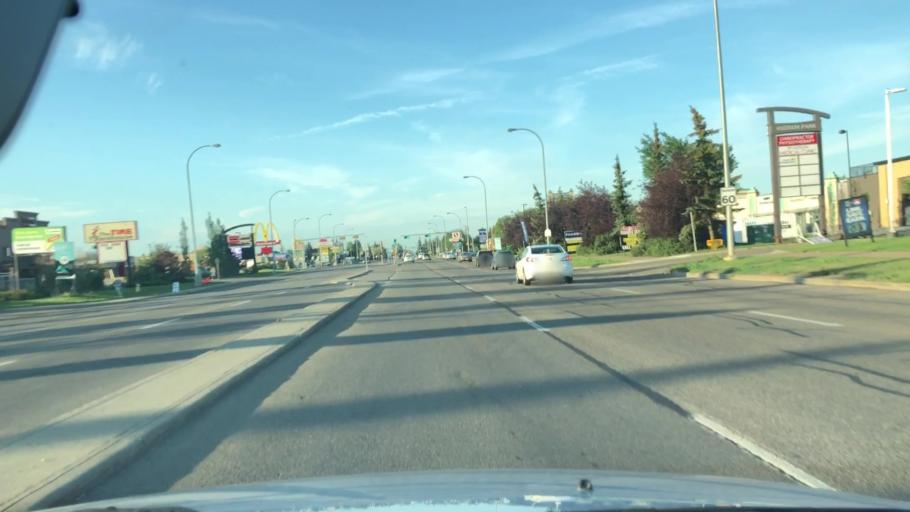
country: CA
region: Alberta
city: Edmonton
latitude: 53.6039
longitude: -113.5413
